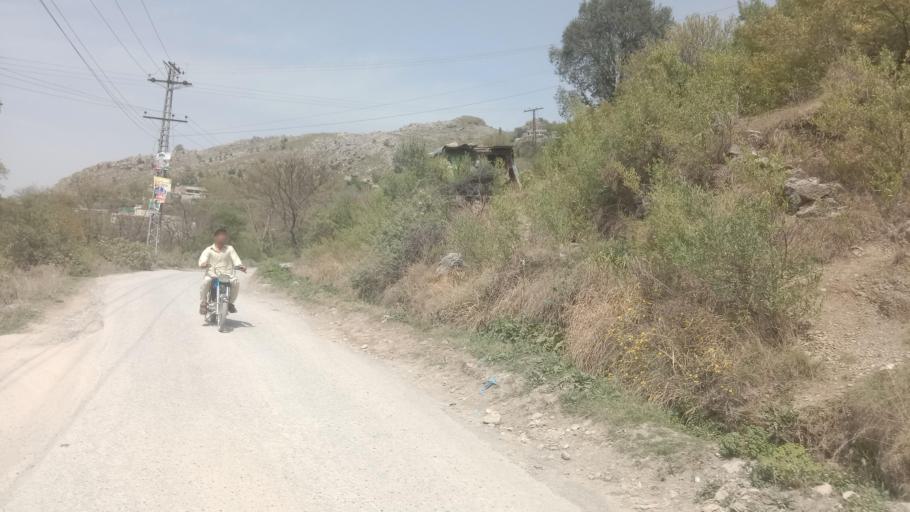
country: PK
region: Khyber Pakhtunkhwa
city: Abbottabad
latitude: 34.1648
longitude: 73.2823
